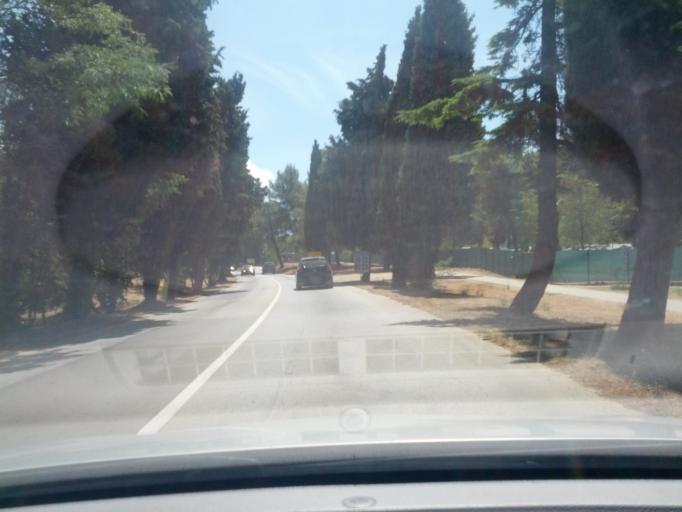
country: HR
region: Istarska
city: Fazana
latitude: 44.9203
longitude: 13.8085
